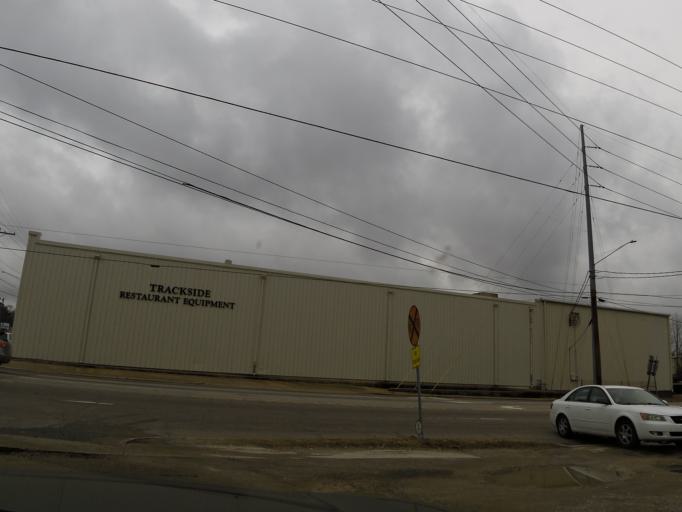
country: US
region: North Carolina
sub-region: Nash County
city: Rocky Mount
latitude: 35.9505
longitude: -77.7935
